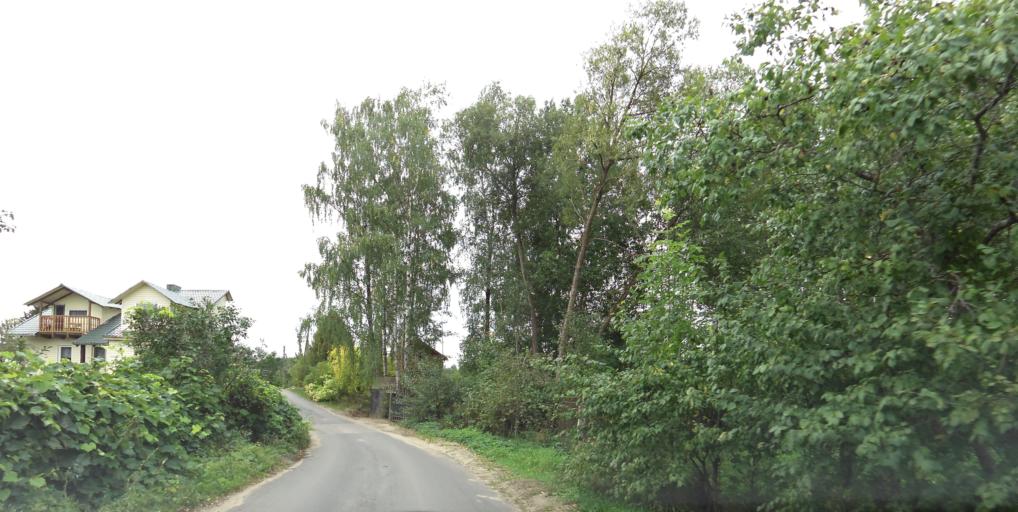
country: LT
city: Grigiskes
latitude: 54.7551
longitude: 25.0281
